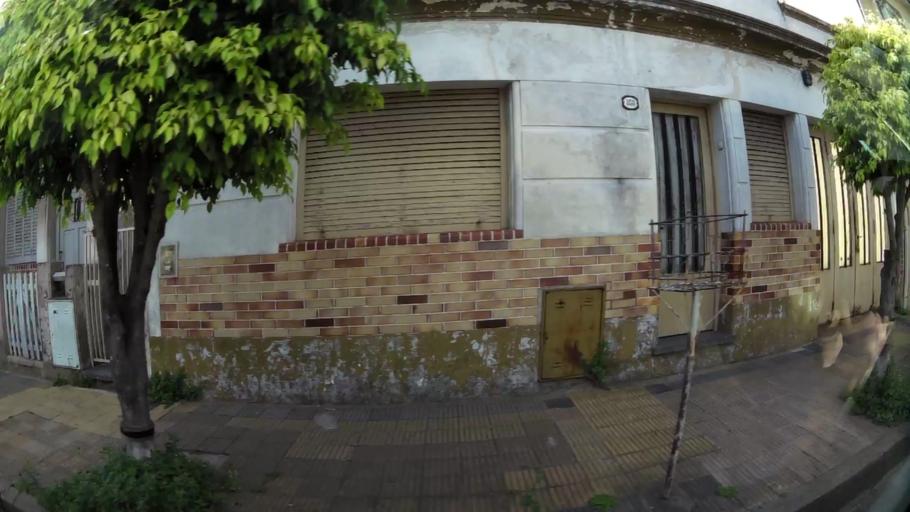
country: AR
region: Buenos Aires
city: San Justo
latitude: -34.6463
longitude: -58.5444
